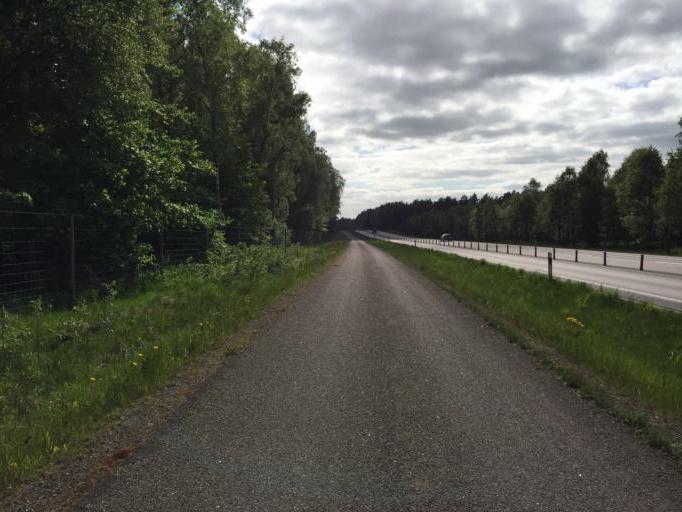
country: SE
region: Skane
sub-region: Sjobo Kommun
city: Blentarp
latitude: 55.6405
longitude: 13.5953
